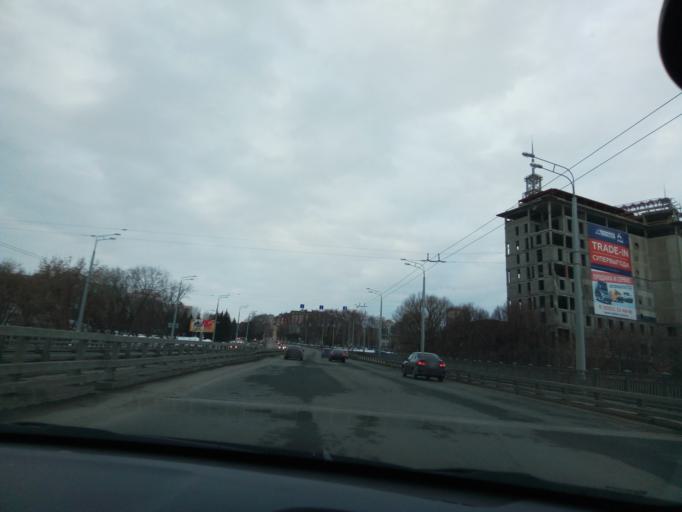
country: RU
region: Chuvashia
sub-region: Cheboksarskiy Rayon
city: Cheboksary
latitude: 56.1453
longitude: 47.2411
